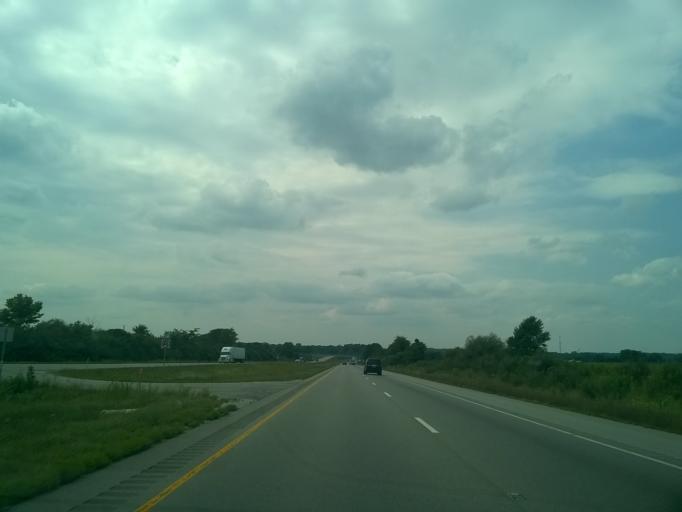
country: US
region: Indiana
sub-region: Putnam County
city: Cloverdale
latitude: 39.5455
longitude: -86.7311
